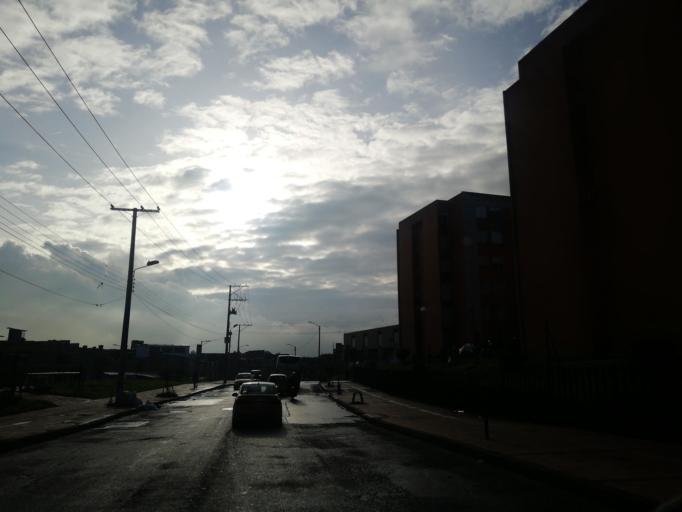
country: CO
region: Cundinamarca
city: Soacha
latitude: 4.5876
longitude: -74.1560
